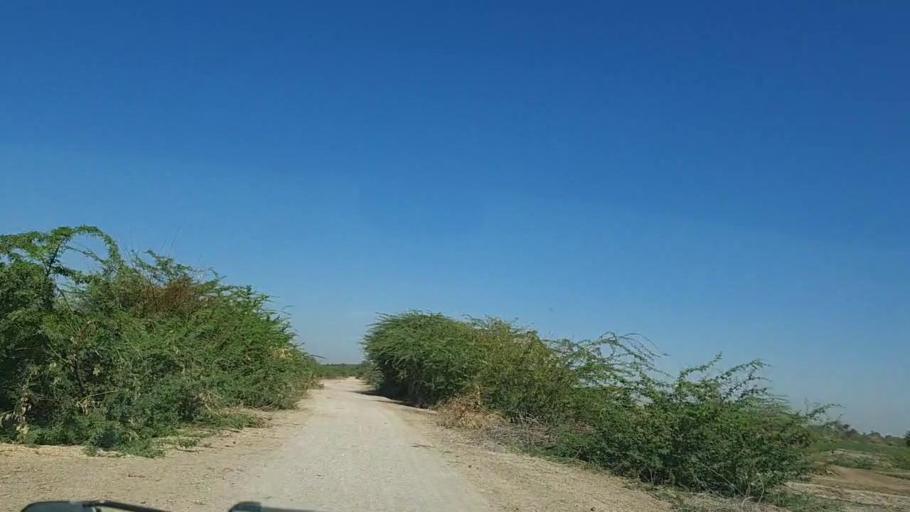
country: PK
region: Sindh
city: Dhoro Naro
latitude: 25.4654
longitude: 69.5131
